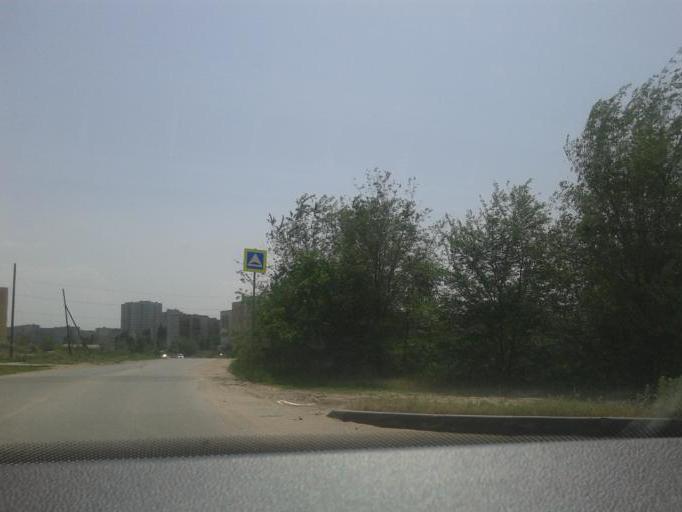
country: RU
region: Volgograd
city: Volgograd
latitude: 48.7648
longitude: 44.4977
